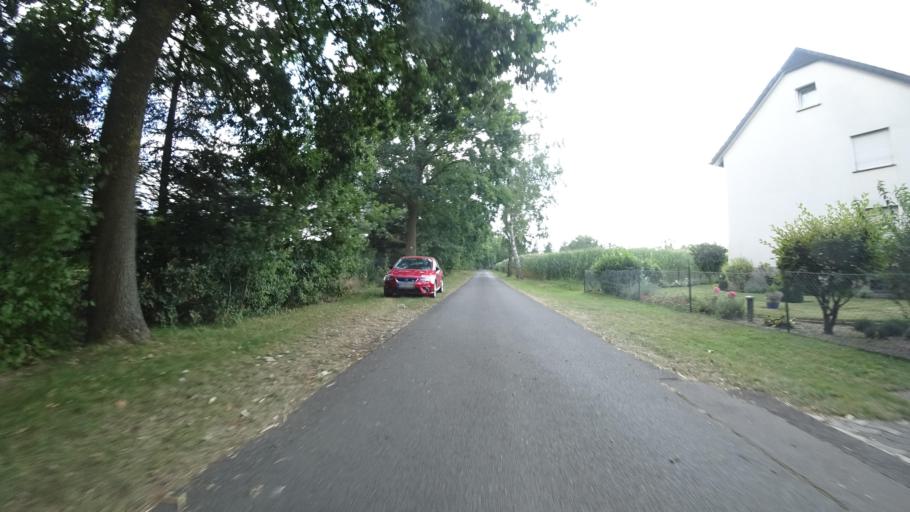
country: DE
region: North Rhine-Westphalia
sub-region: Regierungsbezirk Detmold
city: Guetersloh
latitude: 51.9352
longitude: 8.3767
